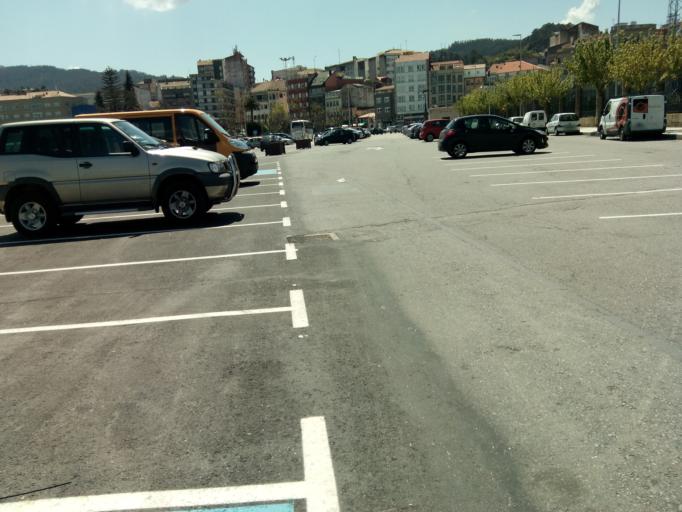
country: ES
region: Galicia
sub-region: Provincia de Pontevedra
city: Marin
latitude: 42.3950
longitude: -8.7024
